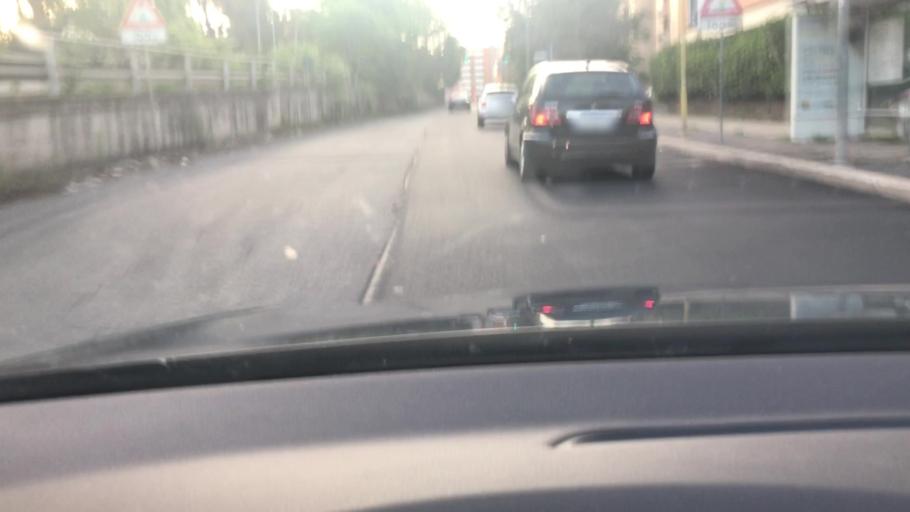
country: IT
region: Latium
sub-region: Citta metropolitana di Roma Capitale
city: Rome
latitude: 41.9287
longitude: 12.5633
